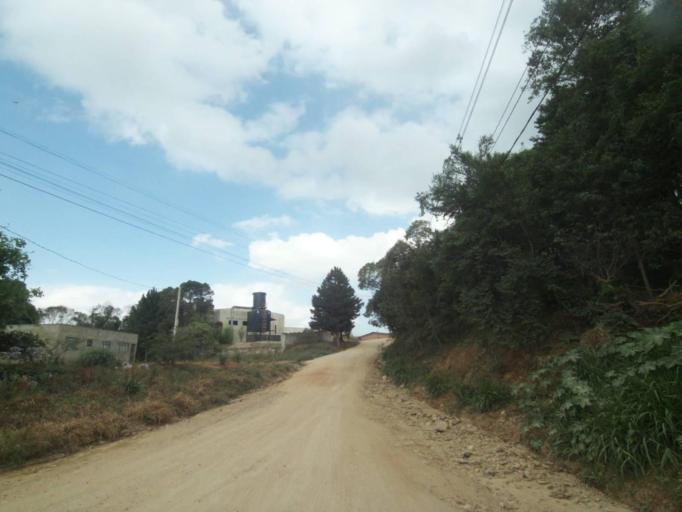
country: BR
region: Parana
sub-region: Araucaria
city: Araucaria
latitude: -25.5163
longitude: -49.3443
